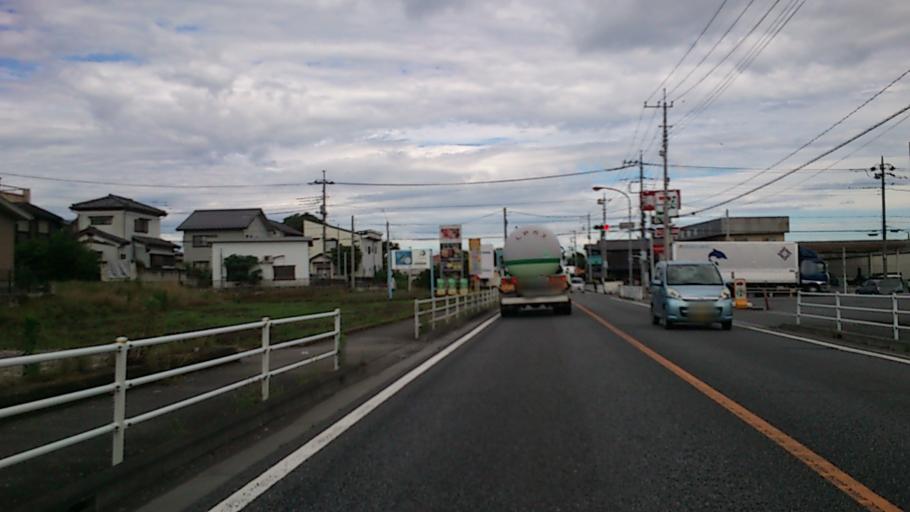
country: JP
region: Saitama
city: Honjo
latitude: 36.2537
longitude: 139.1646
